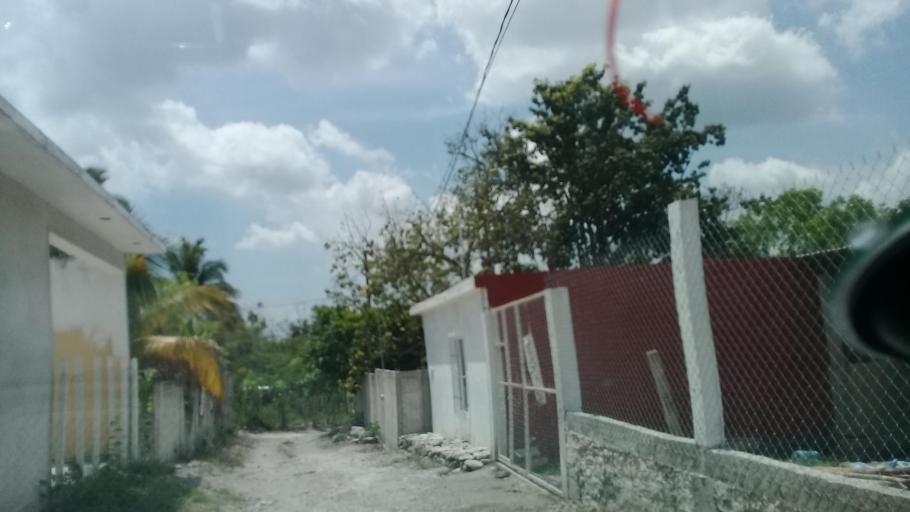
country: MX
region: Veracruz
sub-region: Emiliano Zapata
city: Plan del Rio
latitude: 19.4049
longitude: -96.6544
